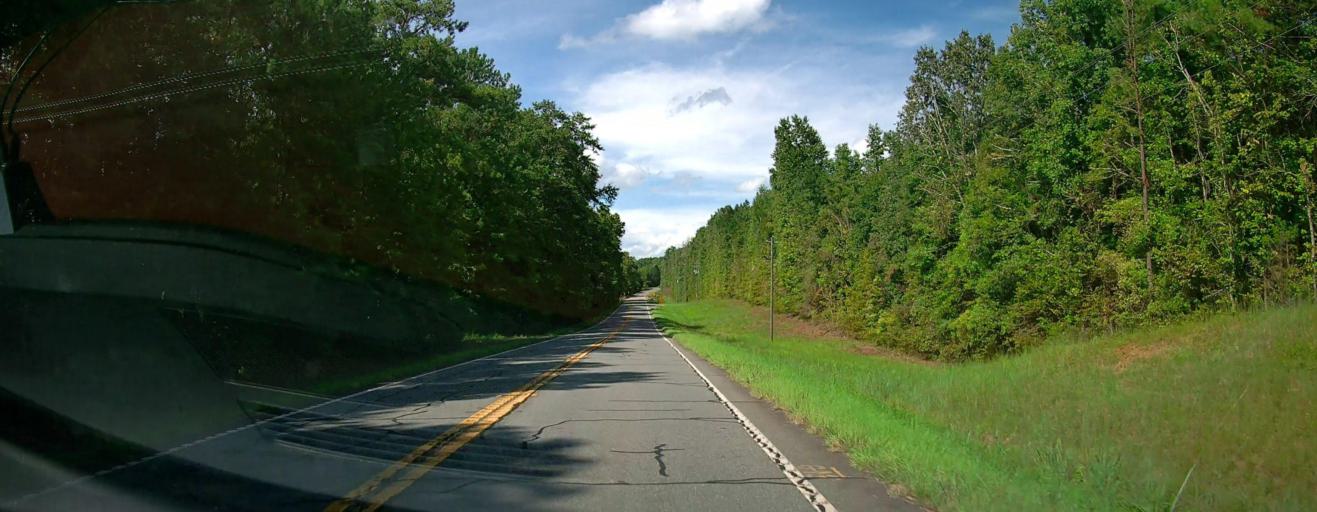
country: US
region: Georgia
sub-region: Talbot County
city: Talbotton
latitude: 32.7389
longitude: -84.5548
